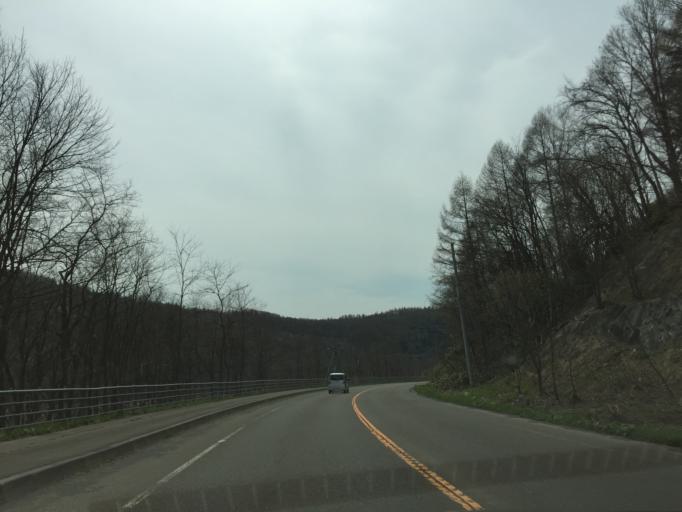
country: JP
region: Hokkaido
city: Ashibetsu
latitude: 43.5538
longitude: 142.1801
